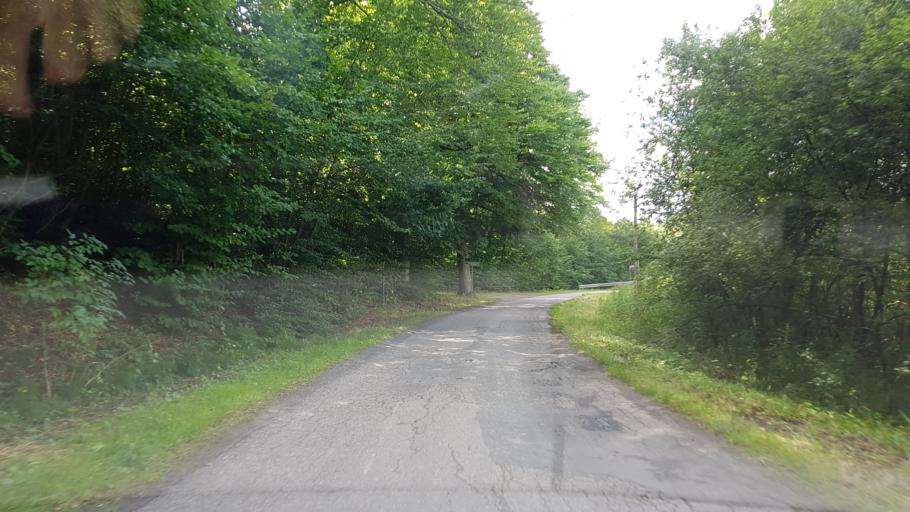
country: PL
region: West Pomeranian Voivodeship
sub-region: Powiat bialogardzki
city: Tychowo
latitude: 53.9888
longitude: 16.3009
